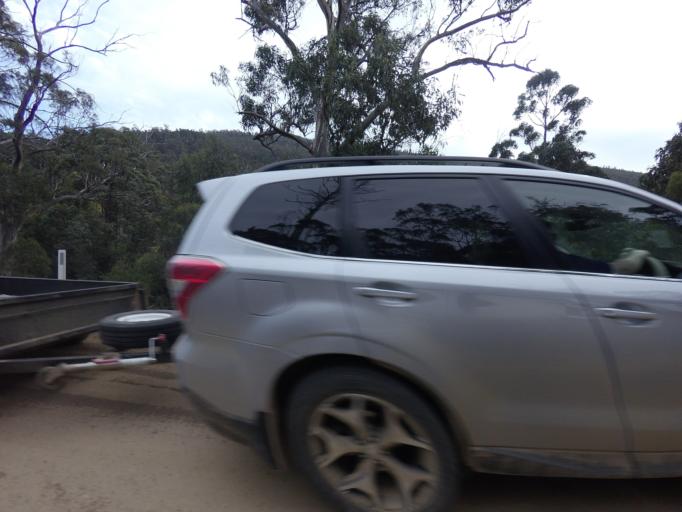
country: AU
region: Tasmania
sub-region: Huon Valley
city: Huonville
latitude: -43.0622
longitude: 147.0939
